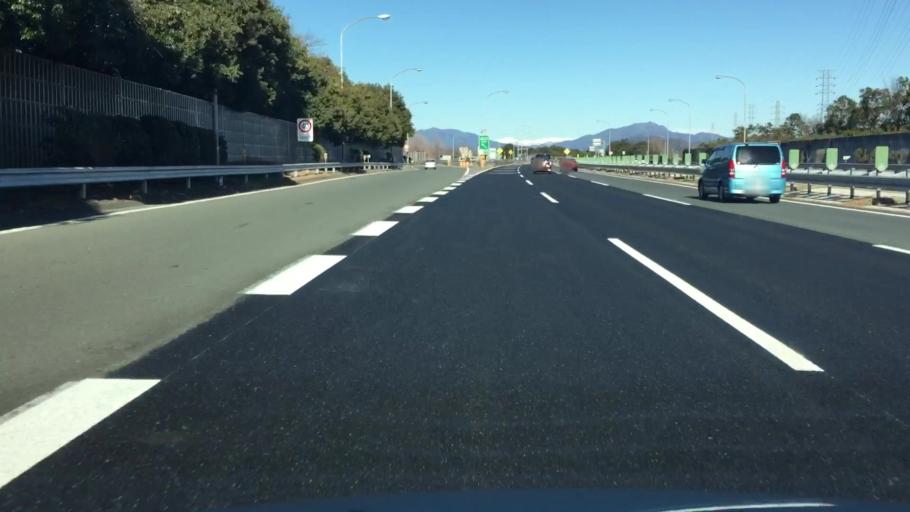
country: JP
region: Gunma
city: Maebashi-shi
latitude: 36.3717
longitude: 139.0287
